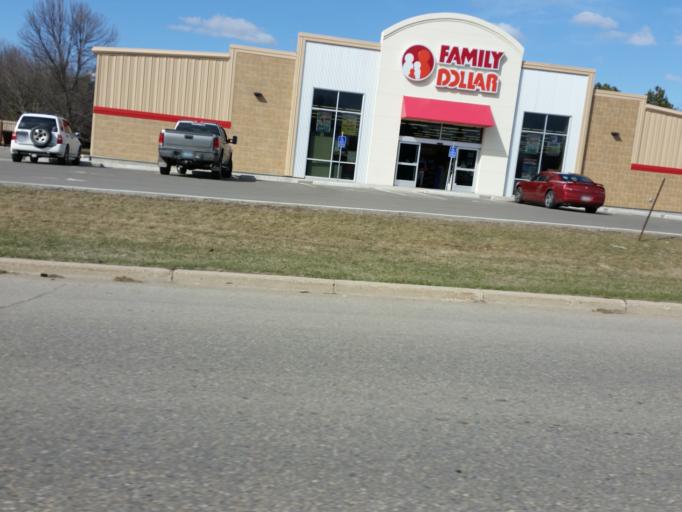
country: US
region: Minnesota
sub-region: Lac qui Parle County
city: Dawson
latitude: 44.9358
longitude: -96.0487
